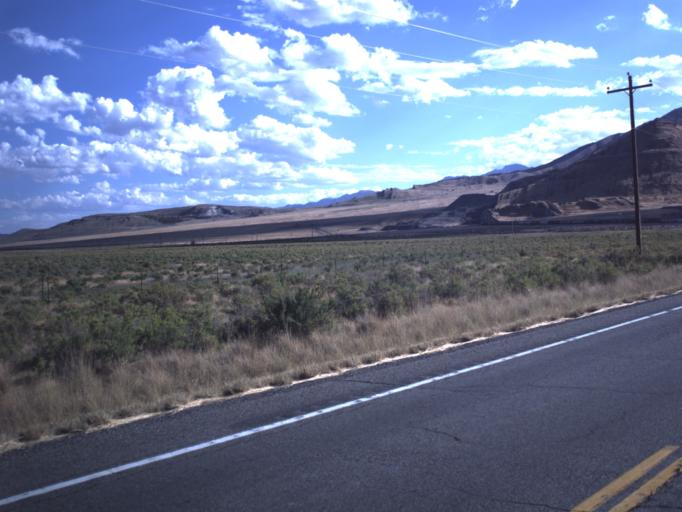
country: US
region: Utah
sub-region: Tooele County
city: Grantsville
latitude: 40.6812
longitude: -112.5478
